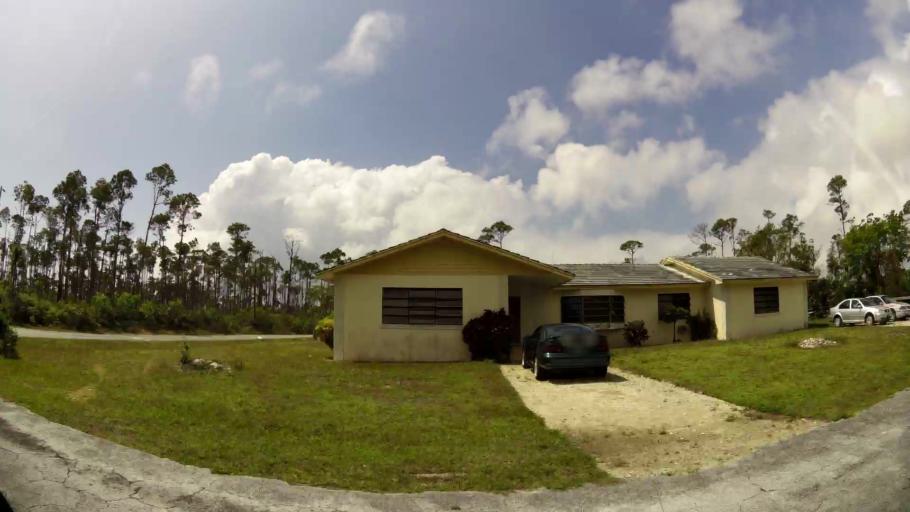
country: BS
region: Freeport
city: Lucaya
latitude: 26.5339
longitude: -78.6238
